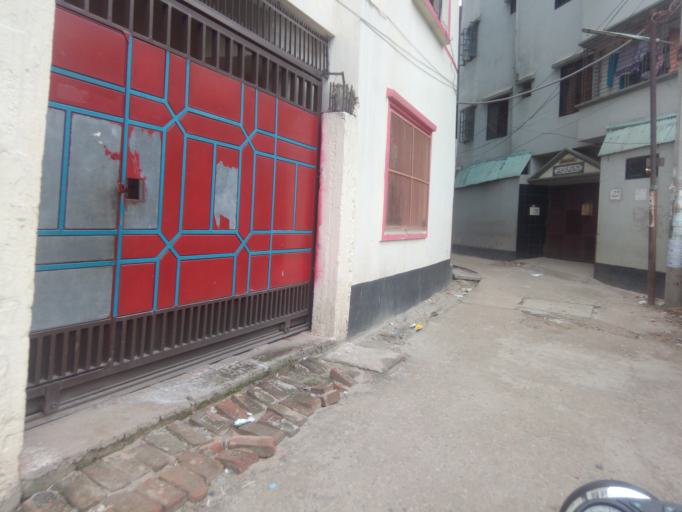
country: BD
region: Dhaka
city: Paltan
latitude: 23.7622
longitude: 90.4225
